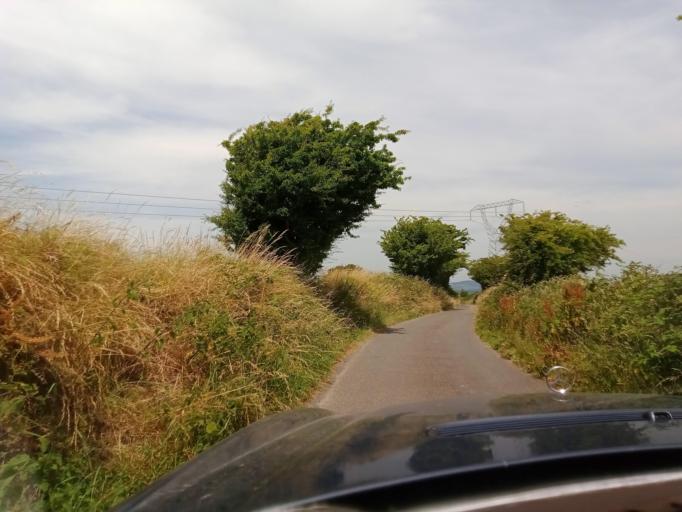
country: IE
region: Leinster
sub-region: Kilkenny
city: Mooncoin
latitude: 52.2625
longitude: -7.2158
